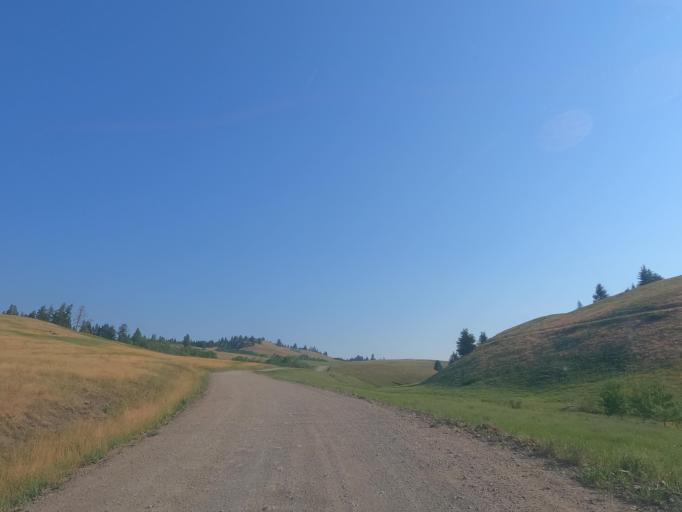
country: CA
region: British Columbia
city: Merritt
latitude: 50.0717
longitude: -120.6556
